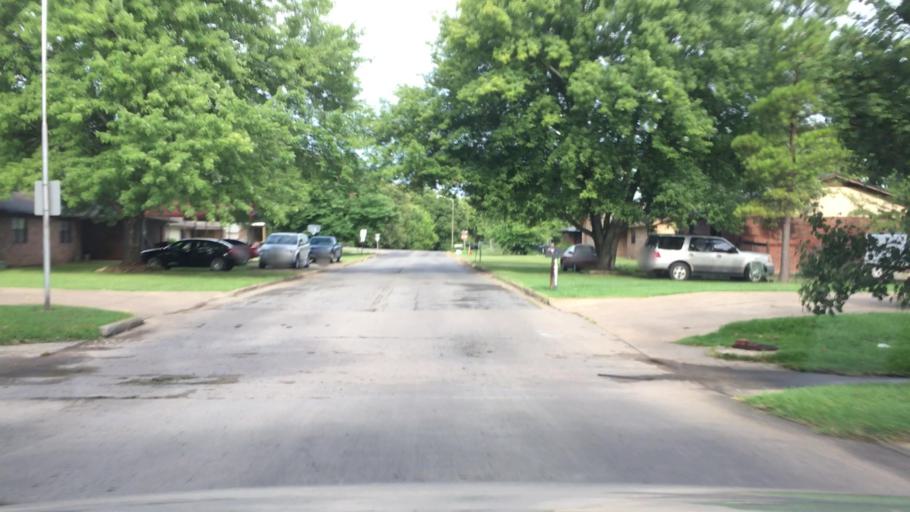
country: US
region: Oklahoma
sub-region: Cherokee County
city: Tahlequah
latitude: 35.9126
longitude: -94.9538
